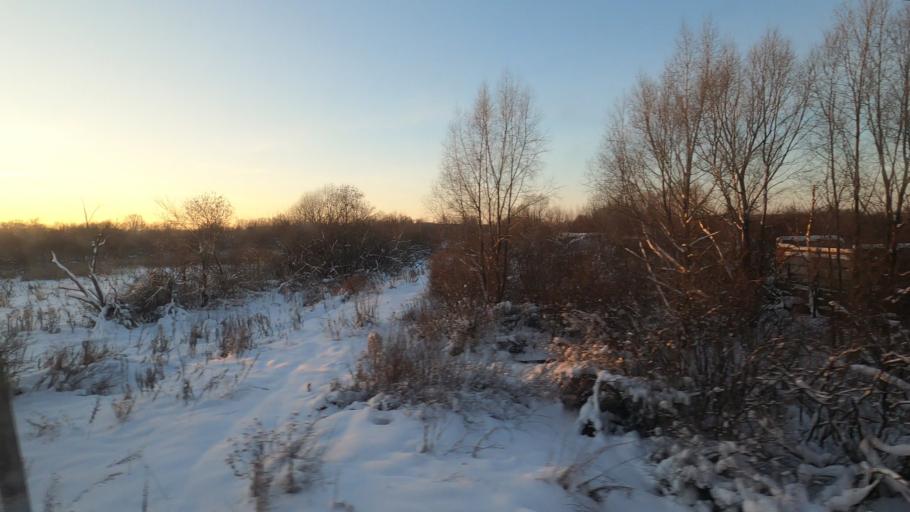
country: RU
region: Moskovskaya
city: Dmitrov
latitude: 56.3592
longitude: 37.5217
